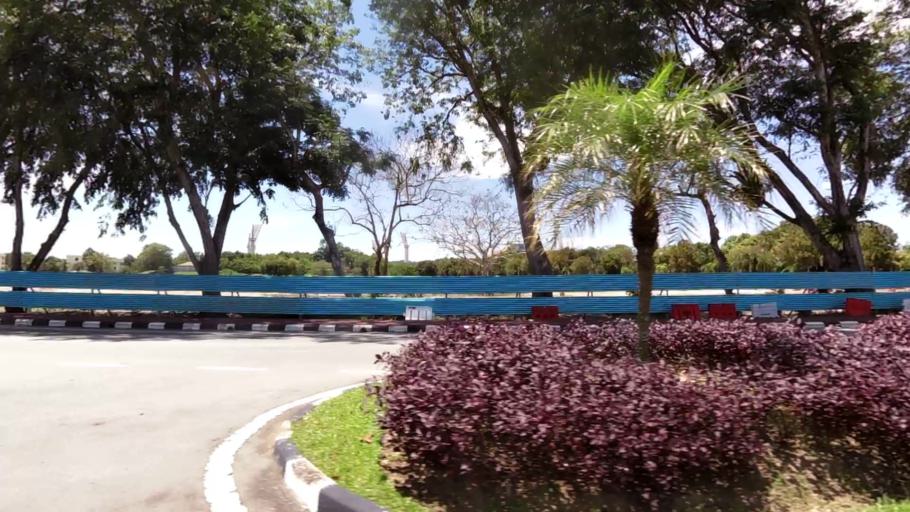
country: BN
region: Brunei and Muara
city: Bandar Seri Begawan
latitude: 4.9301
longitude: 114.9398
